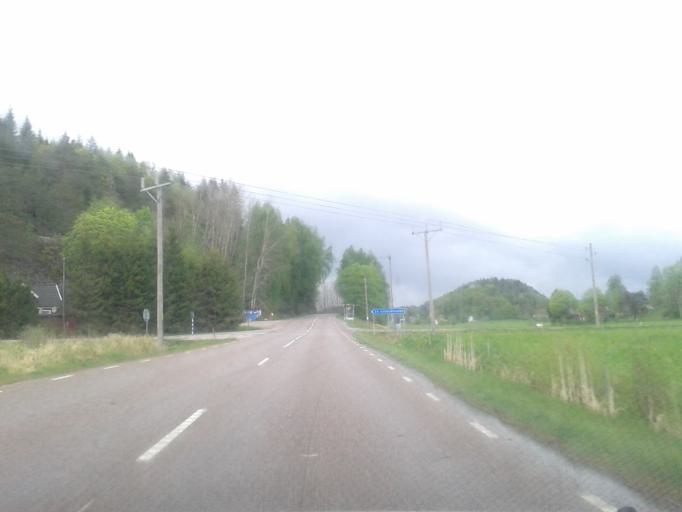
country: SE
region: Vaestra Goetaland
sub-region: Lilla Edets Kommun
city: Lilla Edet
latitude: 58.0990
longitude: 12.1173
